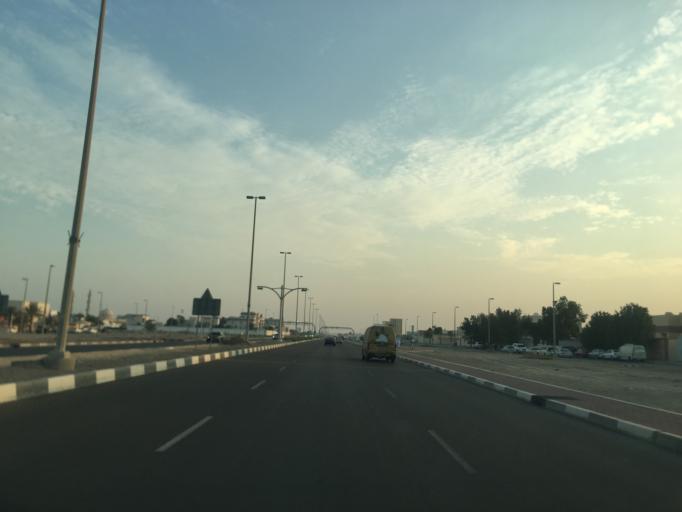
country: AE
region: Abu Dhabi
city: Abu Dhabi
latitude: 24.3091
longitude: 54.6415
